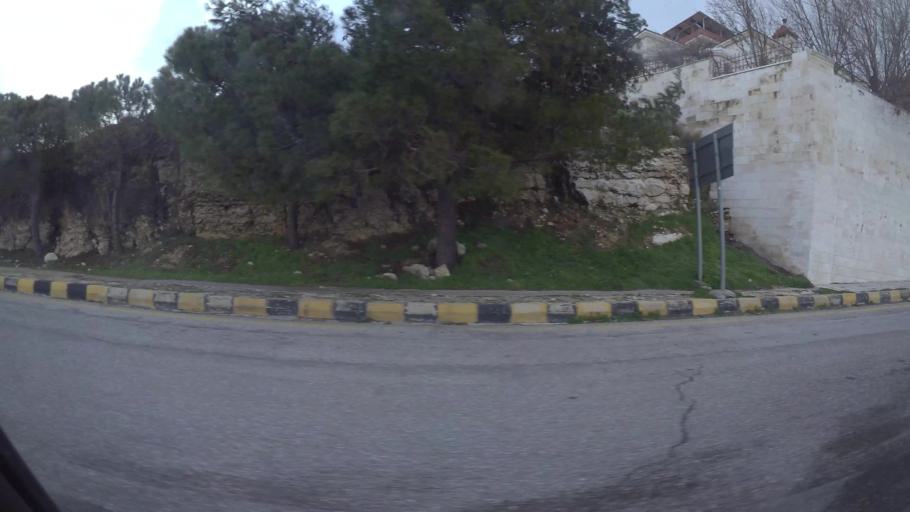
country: JO
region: Amman
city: Al Jubayhah
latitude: 32.0433
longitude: 35.8693
